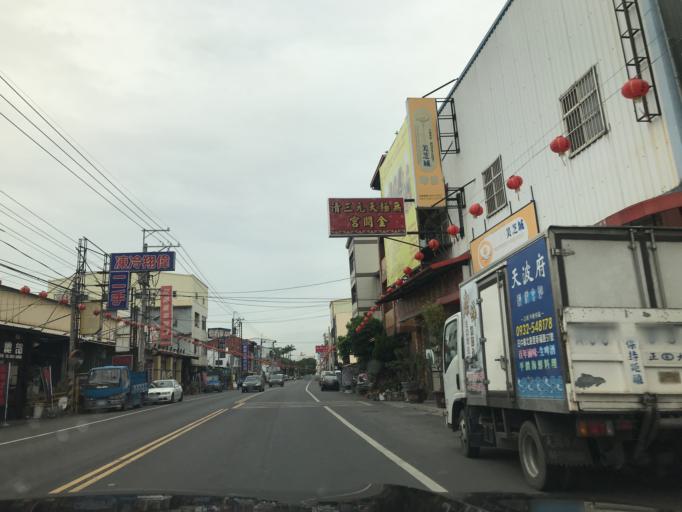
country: TW
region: Taiwan
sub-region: Nantou
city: Nantou
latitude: 23.9363
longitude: 120.5768
